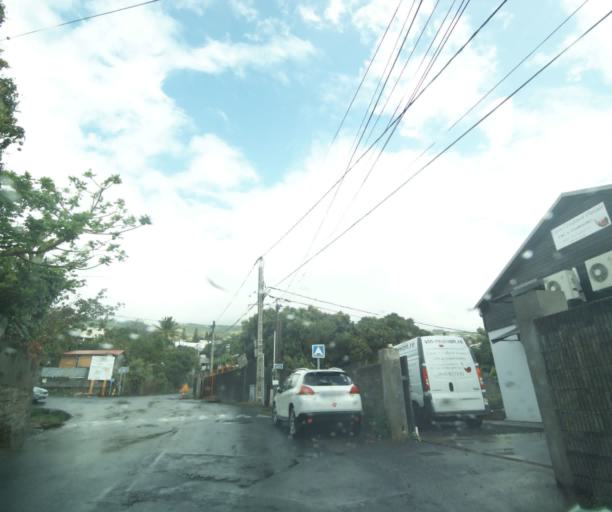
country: RE
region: Reunion
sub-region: Reunion
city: La Possession
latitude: -20.9833
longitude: 55.3292
